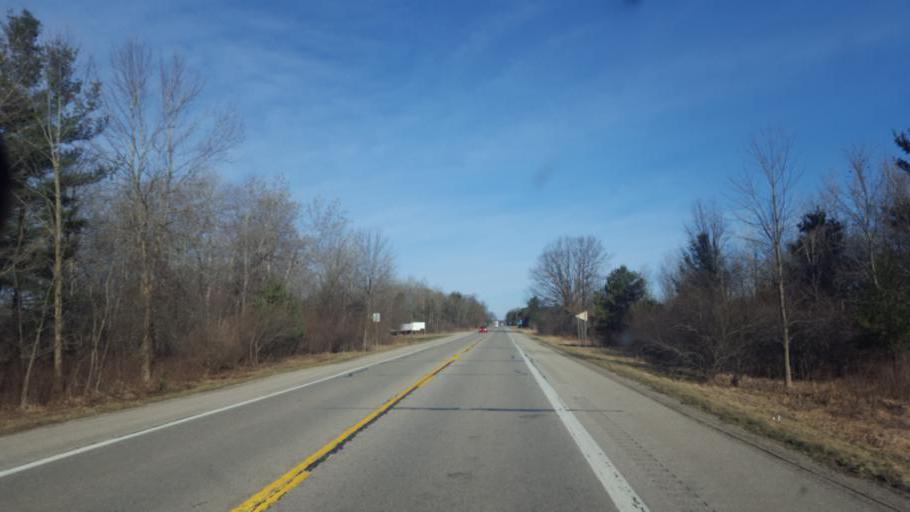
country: US
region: Michigan
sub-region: Montcalm County
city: Edmore
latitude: 43.4103
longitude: -85.1192
